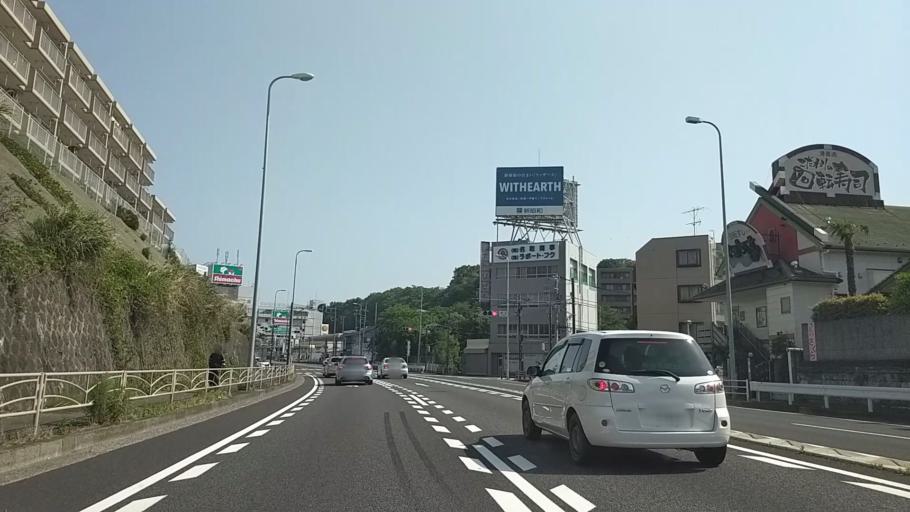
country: JP
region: Kanagawa
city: Yokohama
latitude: 35.4981
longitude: 139.6618
